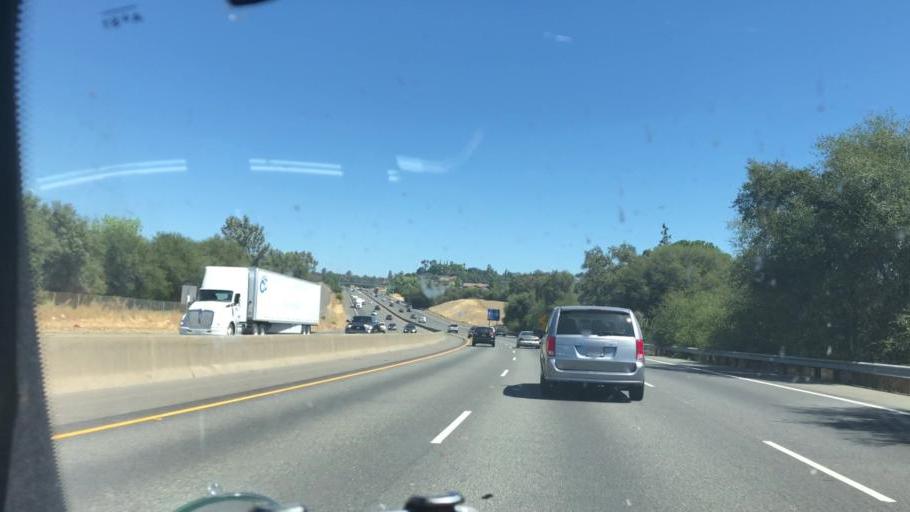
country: US
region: California
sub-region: Placer County
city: Newcastle
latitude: 38.8637
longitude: -121.1331
